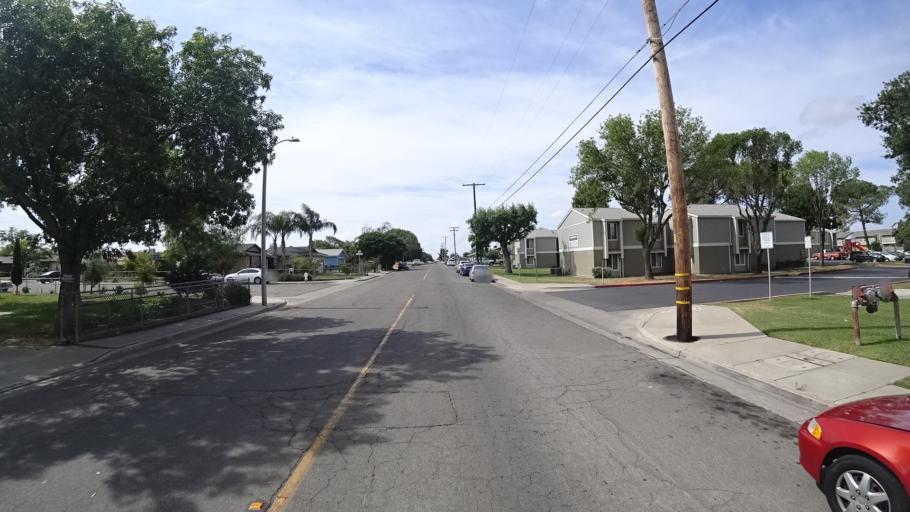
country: US
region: California
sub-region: Kings County
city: Home Garden
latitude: 36.3107
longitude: -119.6528
